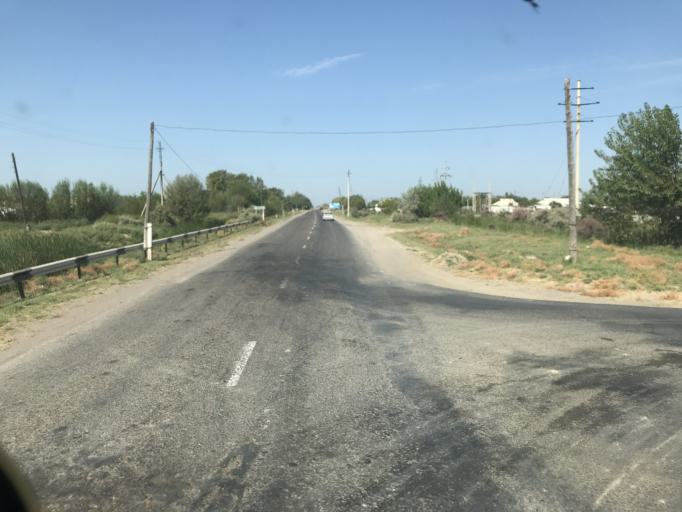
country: KZ
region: Ongtustik Qazaqstan
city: Myrzakent
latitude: 40.6850
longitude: 68.5951
